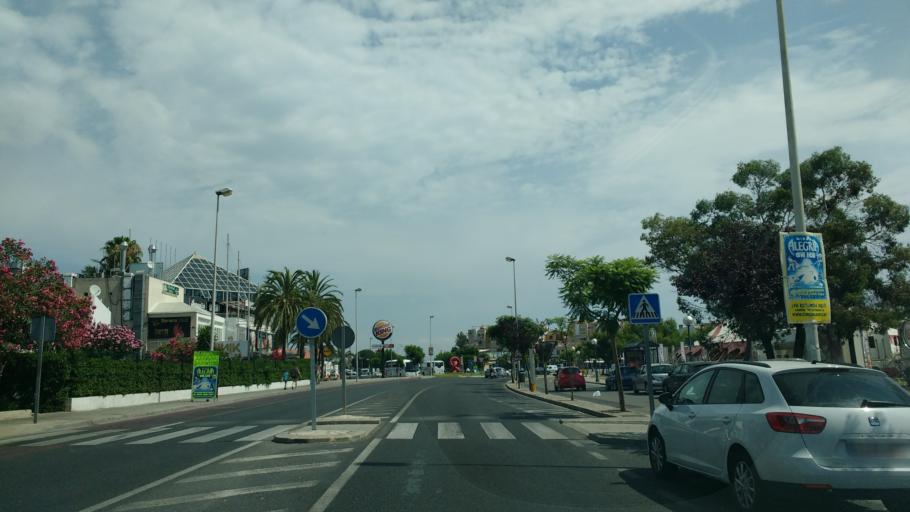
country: ES
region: Balearic Islands
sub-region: Illes Balears
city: Port d'Alcudia
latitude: 39.8386
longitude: 3.1203
